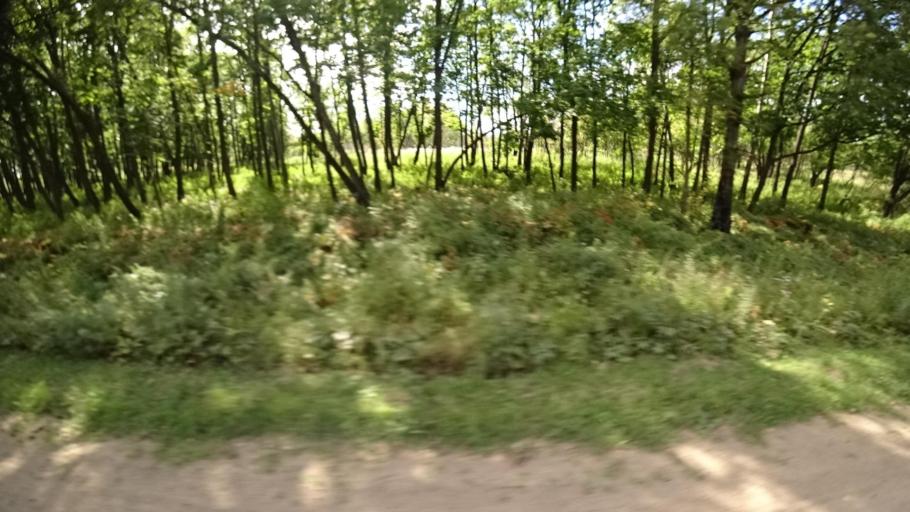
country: RU
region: Primorskiy
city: Yakovlevka
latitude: 44.3829
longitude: 133.5353
